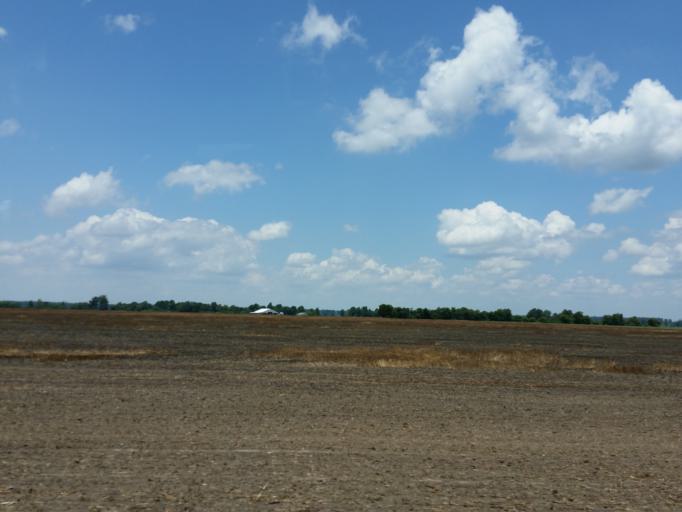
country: US
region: Kentucky
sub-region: Fulton County
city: Hickman
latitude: 36.5474
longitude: -89.3327
